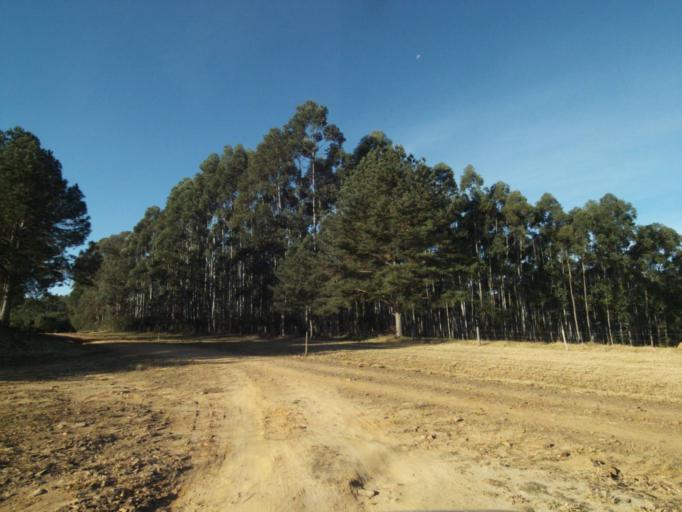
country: BR
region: Parana
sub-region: Telemaco Borba
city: Telemaco Borba
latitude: -24.5148
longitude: -50.6620
